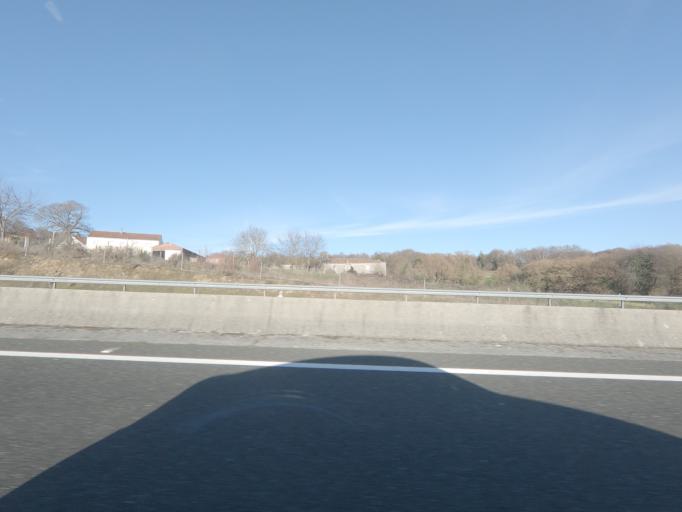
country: ES
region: Galicia
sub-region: Provincia de Pontevedra
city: Lalin
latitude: 42.6478
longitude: -8.1337
